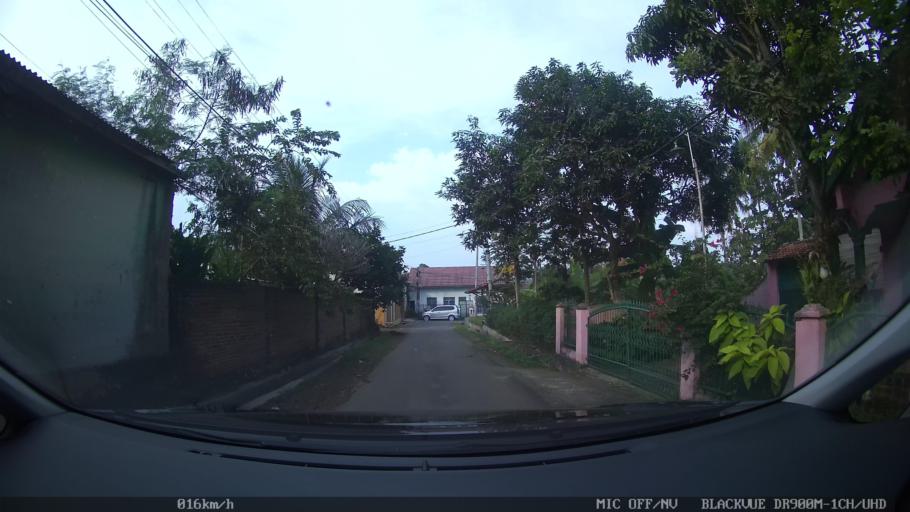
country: ID
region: Lampung
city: Kedaton
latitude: -5.3781
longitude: 105.2393
